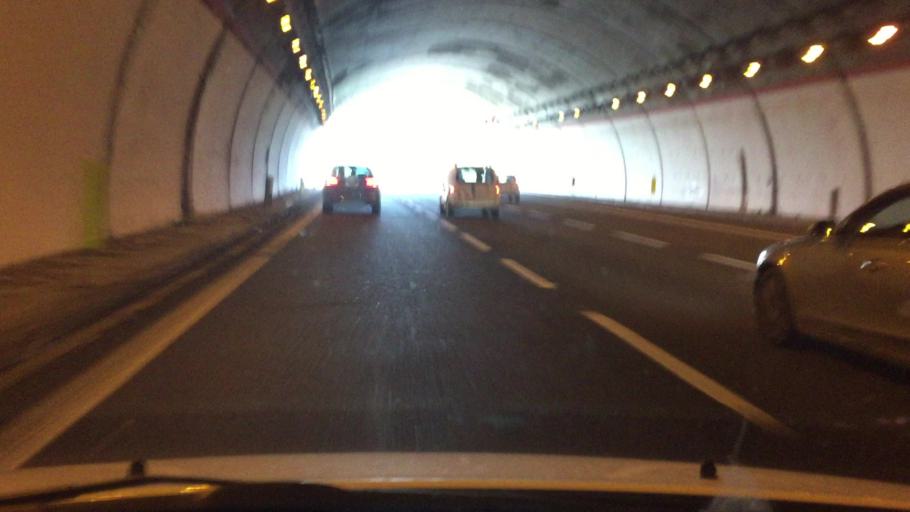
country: VA
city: Vatican City
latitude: 41.9709
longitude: 12.4110
